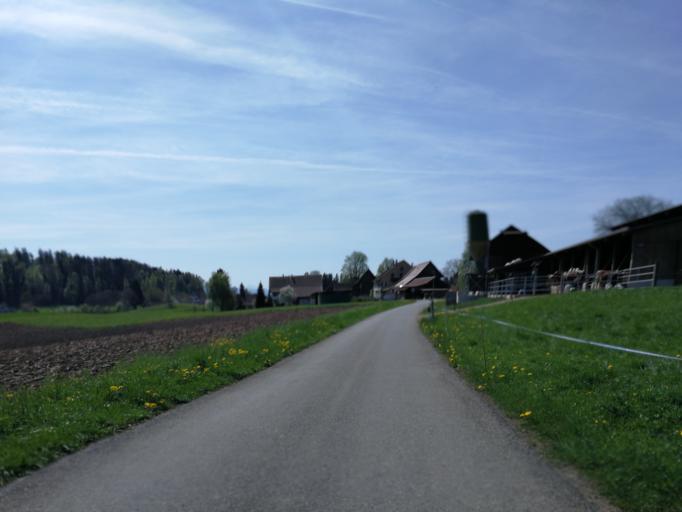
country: CH
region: Zurich
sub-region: Bezirk Hinwil
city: Bubikon
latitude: 47.2755
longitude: 8.8095
